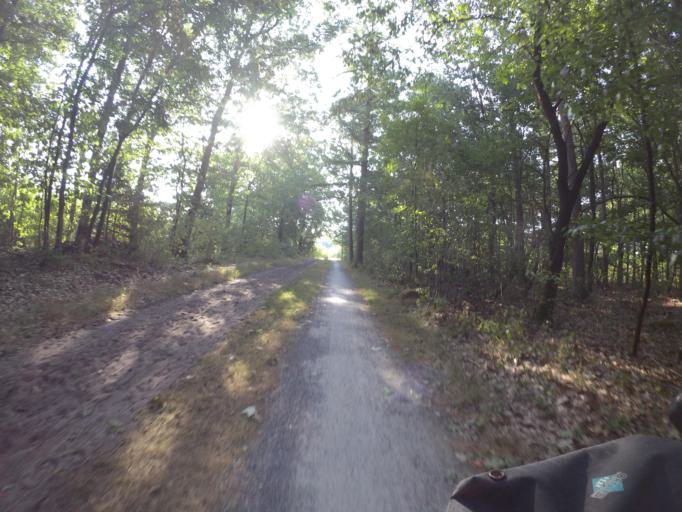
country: NL
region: Drenthe
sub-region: Gemeente Westerveld
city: Dwingeloo
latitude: 52.9230
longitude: 6.3261
